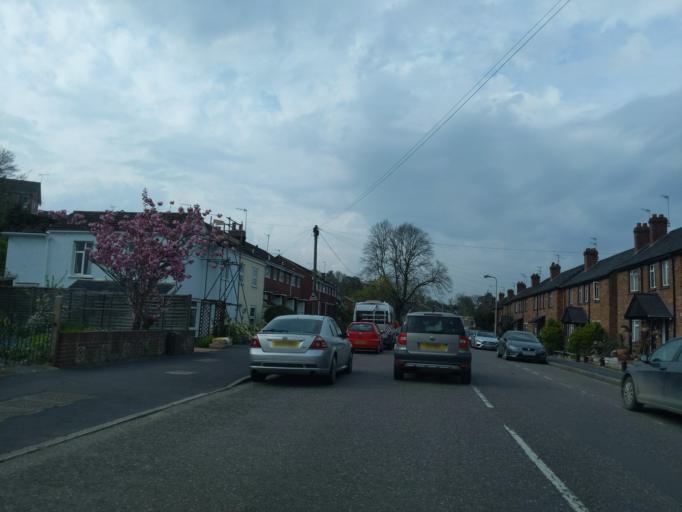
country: GB
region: England
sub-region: Devon
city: Exeter
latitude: 50.7278
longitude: -3.5491
